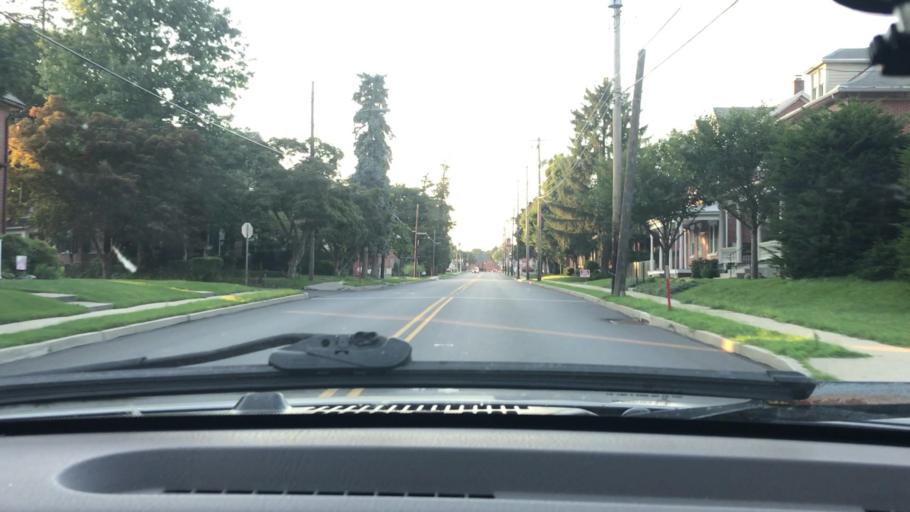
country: US
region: Pennsylvania
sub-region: Lancaster County
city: East Petersburg
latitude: 40.0968
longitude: -76.3524
